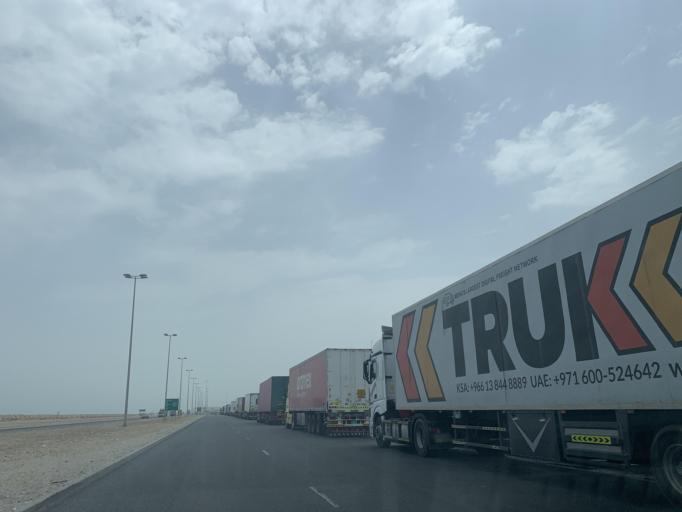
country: BH
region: Muharraq
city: Al Hadd
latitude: 26.2024
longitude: 50.7087
